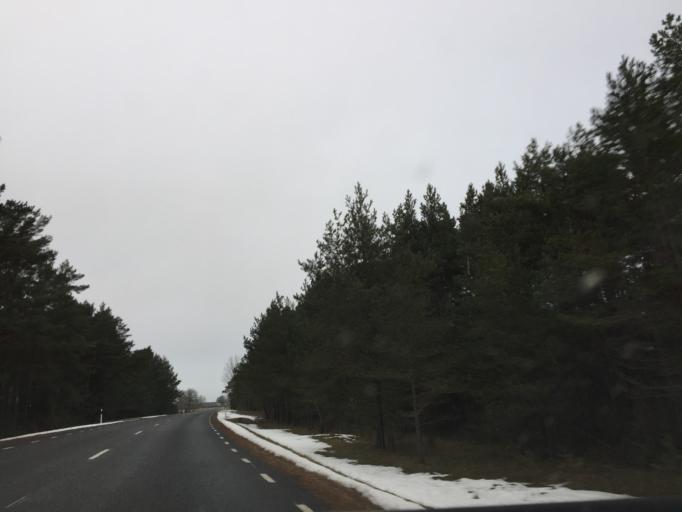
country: EE
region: Saare
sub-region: Kuressaare linn
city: Kuressaare
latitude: 58.5565
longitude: 22.3155
